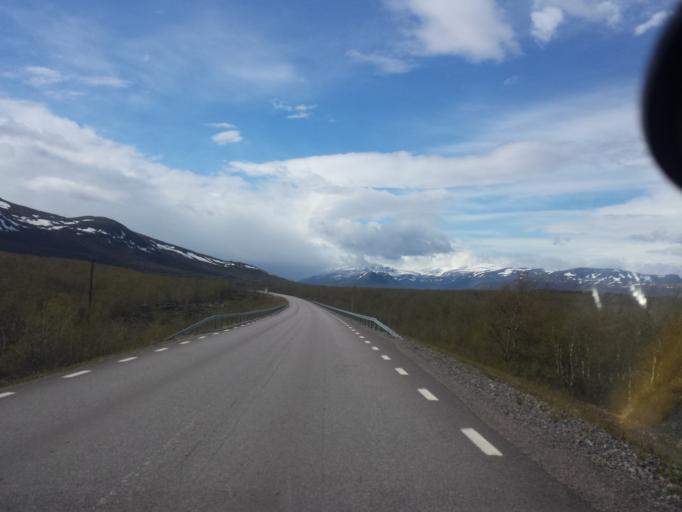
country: SE
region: Norrbotten
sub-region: Kiruna Kommun
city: Kiruna
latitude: 68.1885
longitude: 19.7868
